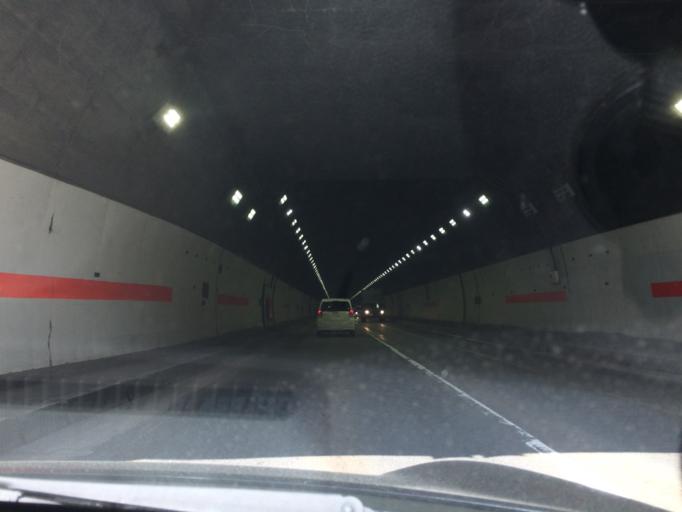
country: JP
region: Hokkaido
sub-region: Asahikawa-shi
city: Asahikawa
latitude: 43.7390
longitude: 142.2429
